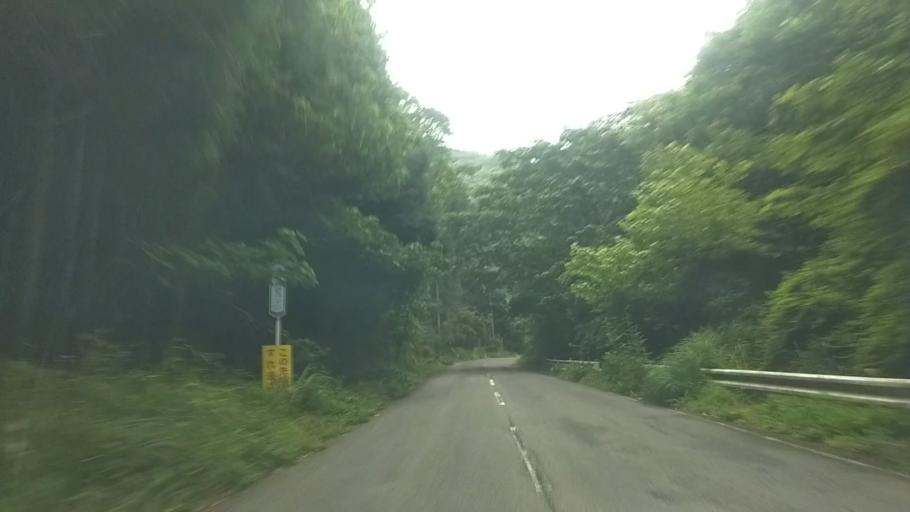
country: JP
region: Chiba
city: Kawaguchi
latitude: 35.2202
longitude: 140.1404
